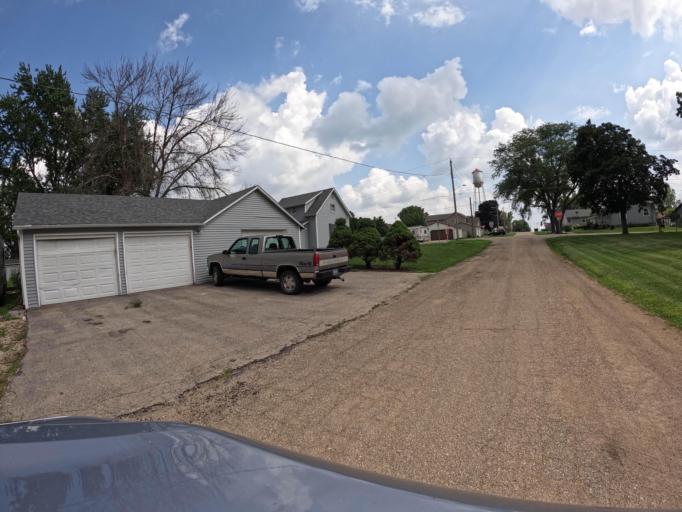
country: US
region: Iowa
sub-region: Clinton County
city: Camanche
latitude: 41.8024
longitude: -90.3577
